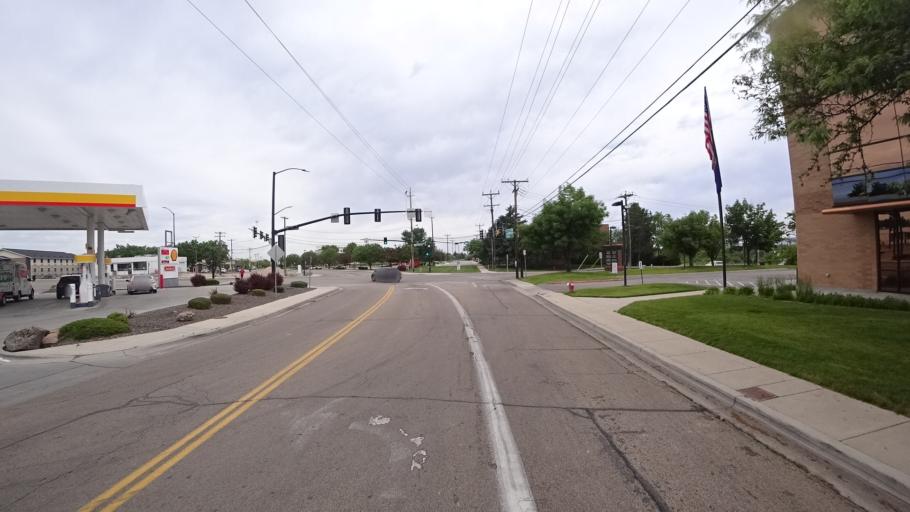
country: US
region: Idaho
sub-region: Ada County
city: Boise
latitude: 43.5736
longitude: -116.2139
